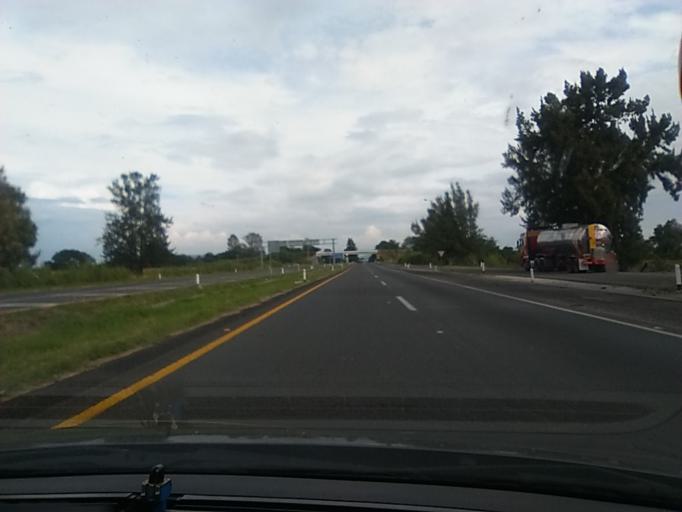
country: MX
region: Michoacan
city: Vistahermosa de Negrete
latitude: 20.2874
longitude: -102.4662
